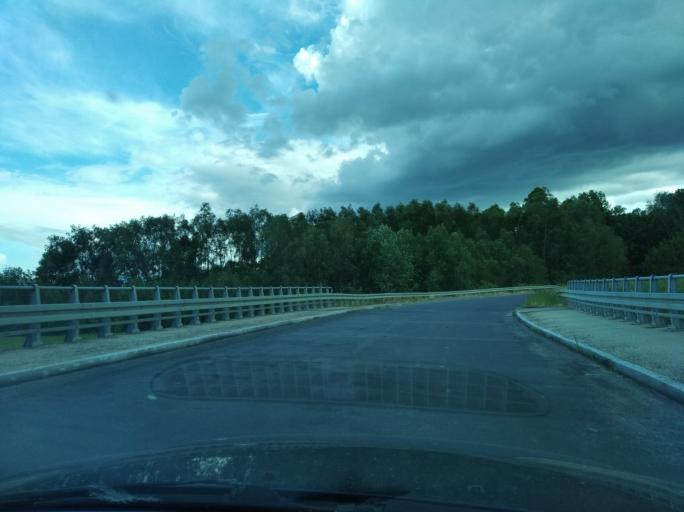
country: PL
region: Subcarpathian Voivodeship
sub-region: Powiat jaroslawski
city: Rokietnica
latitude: 49.9422
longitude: 22.6664
